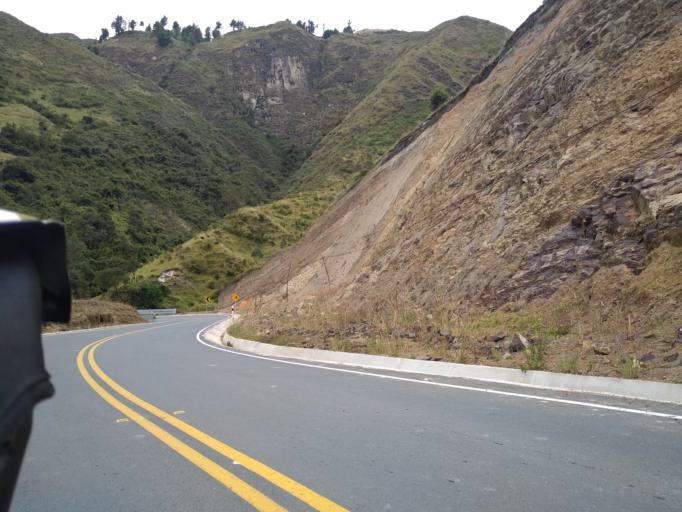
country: EC
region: Cotopaxi
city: Saquisili
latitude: -0.7569
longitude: -78.9140
